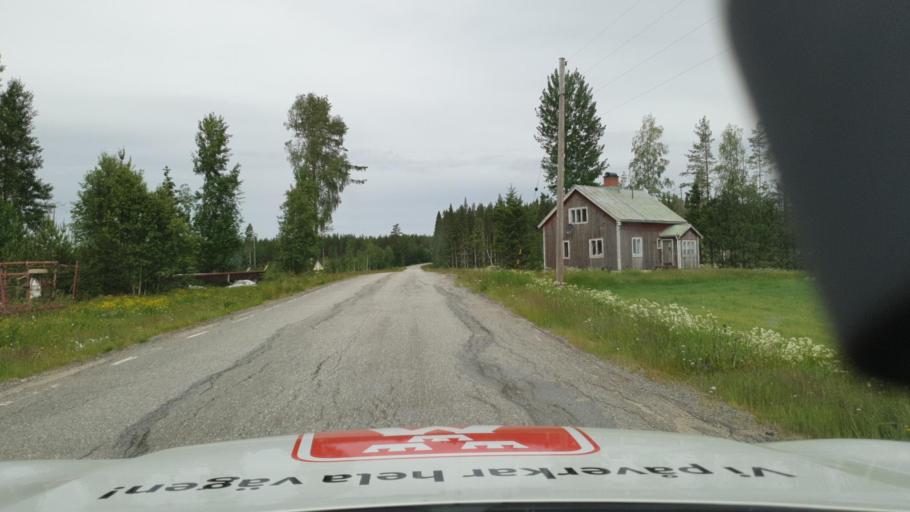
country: SE
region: Vaesterbotten
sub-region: Robertsfors Kommun
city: Robertsfors
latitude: 64.2864
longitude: 20.6531
